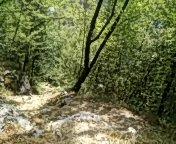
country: IT
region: Tuscany
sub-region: Provincia di Lucca
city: Pontestazzemese
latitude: 43.9952
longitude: 10.3346
